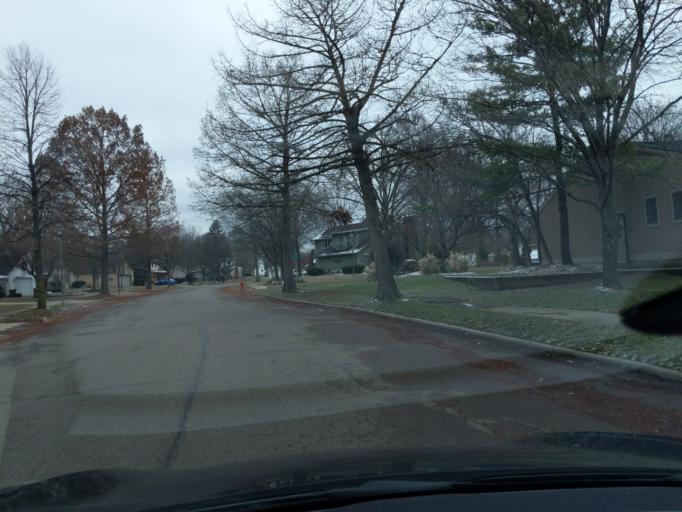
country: US
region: Michigan
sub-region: Ingham County
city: East Lansing
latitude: 42.7542
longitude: -84.5113
